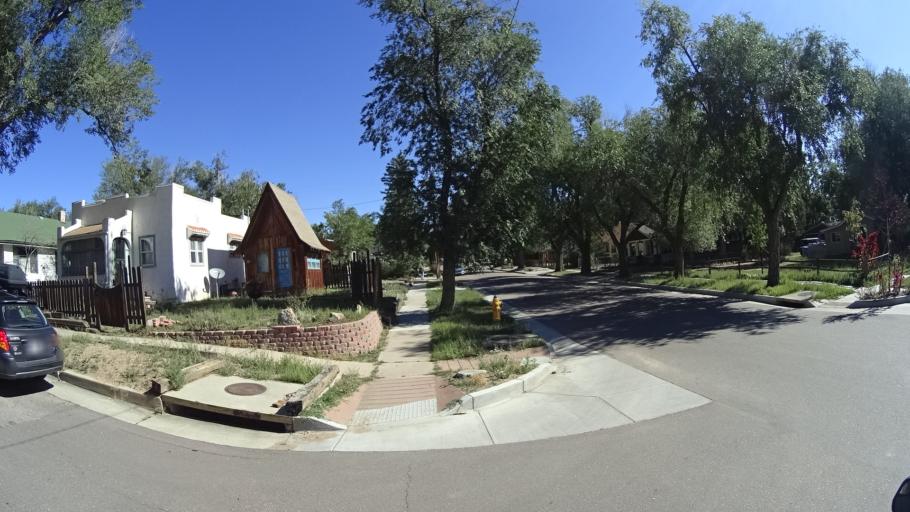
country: US
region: Colorado
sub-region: El Paso County
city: Colorado Springs
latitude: 38.8491
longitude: -104.8585
